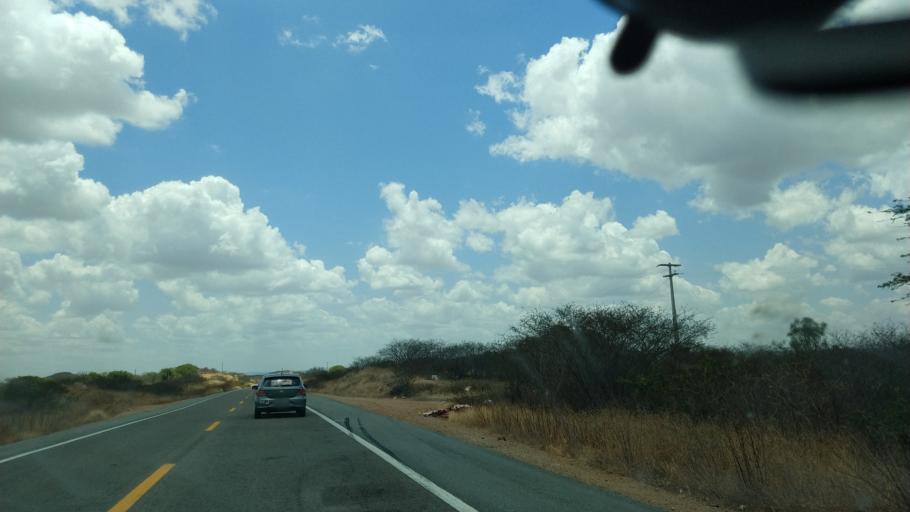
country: BR
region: Rio Grande do Norte
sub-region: Cerro Cora
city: Cerro Cora
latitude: -6.2094
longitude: -36.3090
